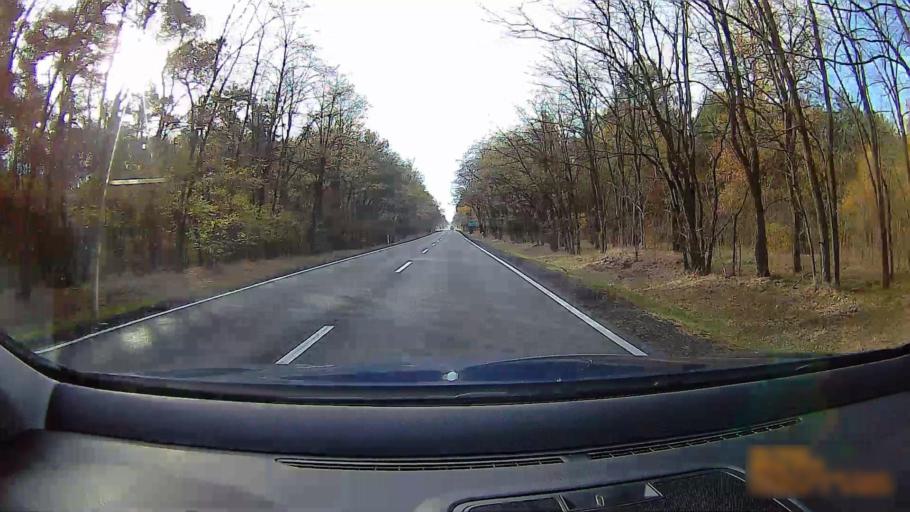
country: PL
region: Greater Poland Voivodeship
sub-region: Powiat koninski
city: Rychwal
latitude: 52.0345
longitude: 18.1621
